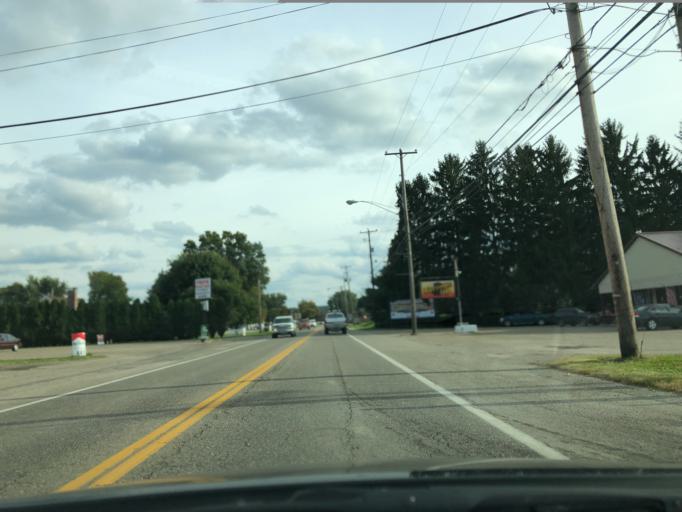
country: US
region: Ohio
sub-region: Tuscarawas County
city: Strasburg
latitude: 40.6089
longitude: -81.5334
